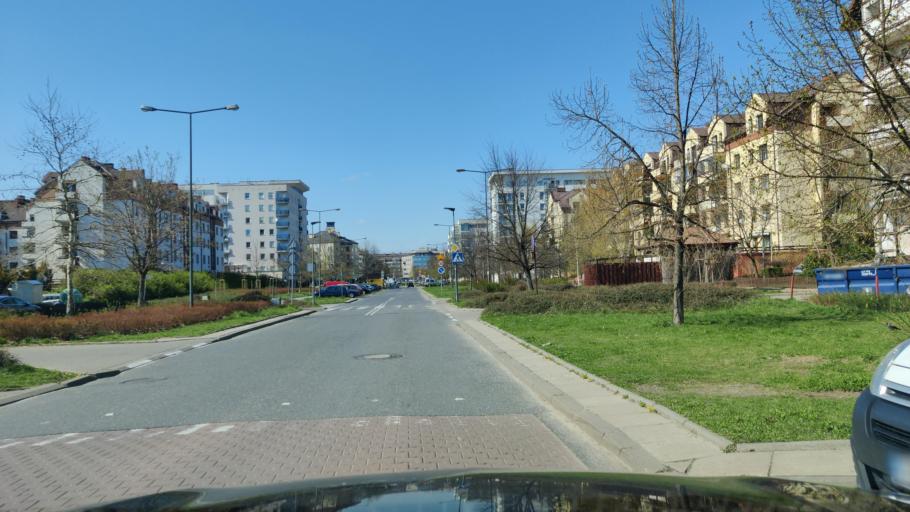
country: PL
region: Masovian Voivodeship
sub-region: Warszawa
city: Kabaty
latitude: 52.1302
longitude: 21.0727
